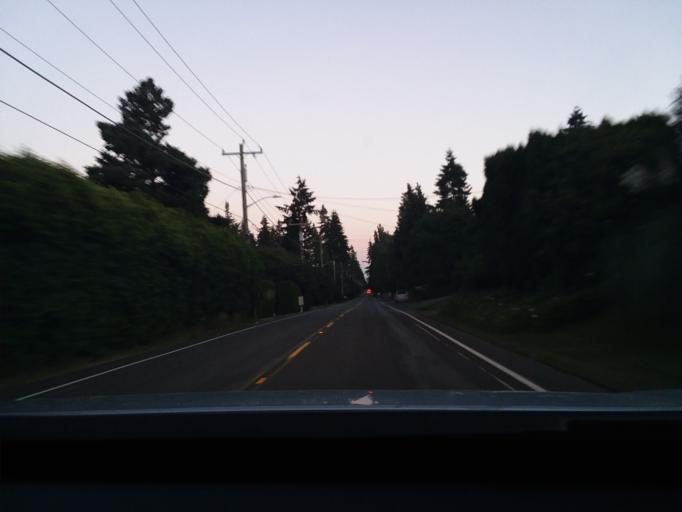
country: US
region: Washington
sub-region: King County
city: Shoreline
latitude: 47.7596
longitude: -122.3404
